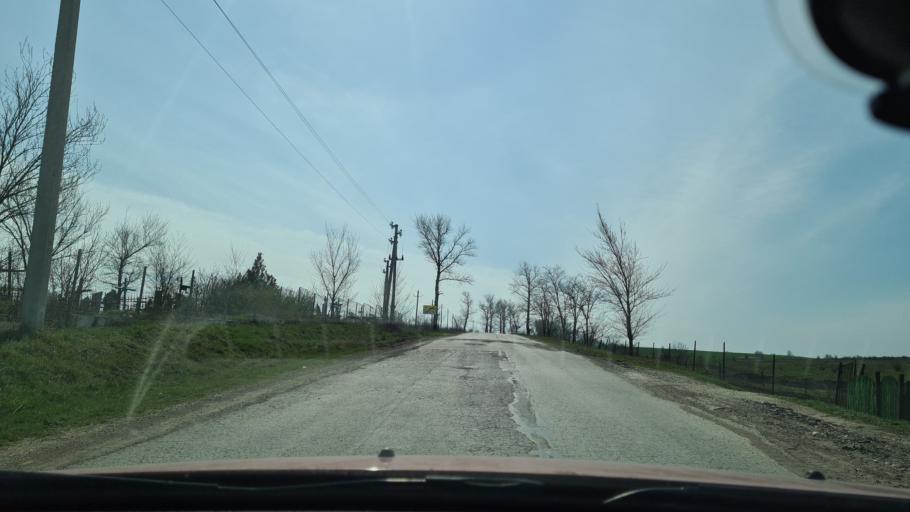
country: MD
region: Ungheni
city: Ungheni
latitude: 47.3161
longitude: 27.9022
